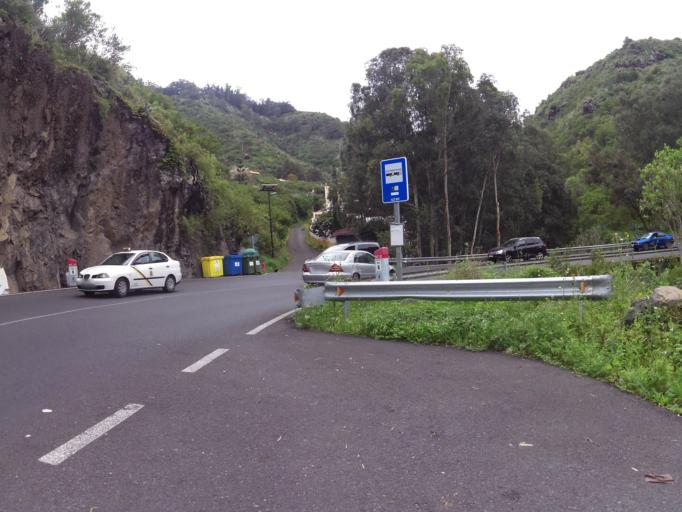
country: ES
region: Canary Islands
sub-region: Provincia de Las Palmas
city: Teror
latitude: 28.0768
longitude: -15.5178
